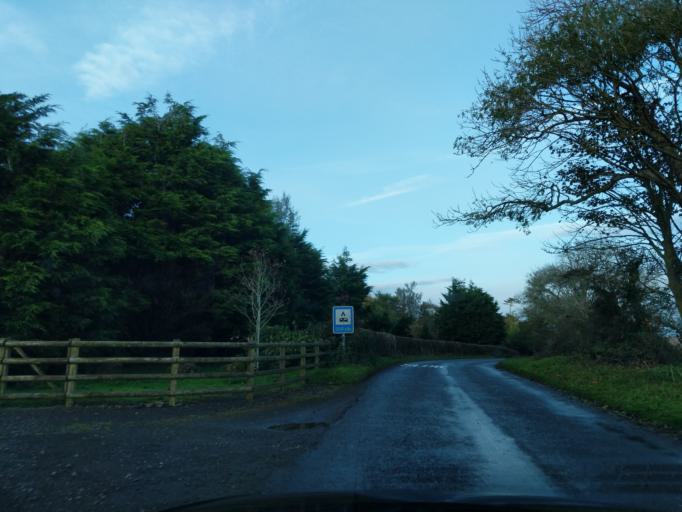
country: GB
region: Scotland
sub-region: Dumfries and Galloway
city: Kirkcudbright
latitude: 54.8173
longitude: -4.0851
